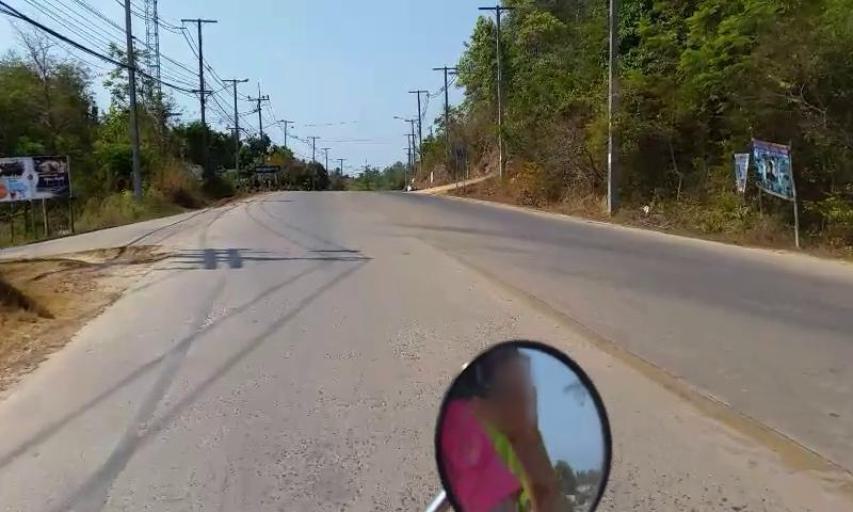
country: TH
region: Krabi
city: Saladan
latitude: 7.6198
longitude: 99.0321
